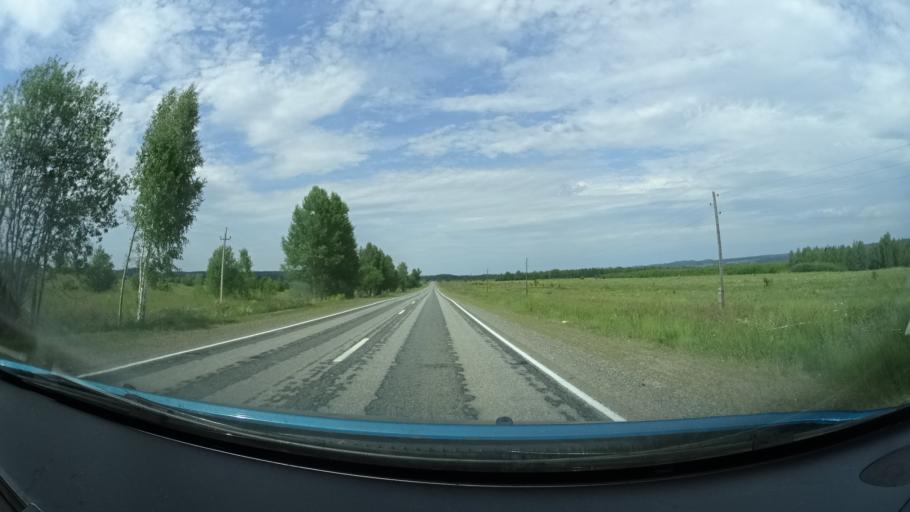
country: RU
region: Perm
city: Osa
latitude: 57.1310
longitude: 55.5257
